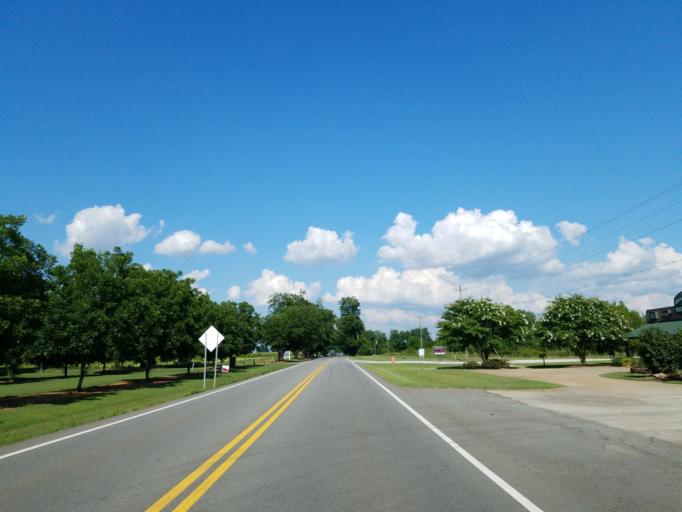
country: US
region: Georgia
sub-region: Peach County
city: Fort Valley
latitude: 32.5539
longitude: -83.8170
